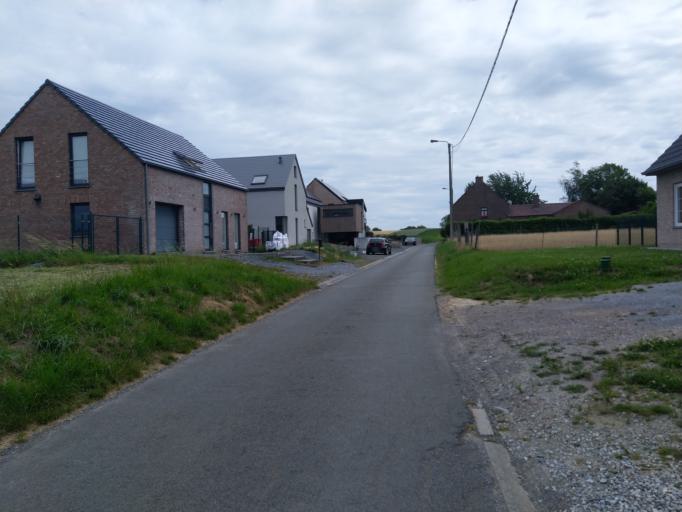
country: BE
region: Wallonia
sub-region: Province du Hainaut
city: Jurbise
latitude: 50.5191
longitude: 3.8562
